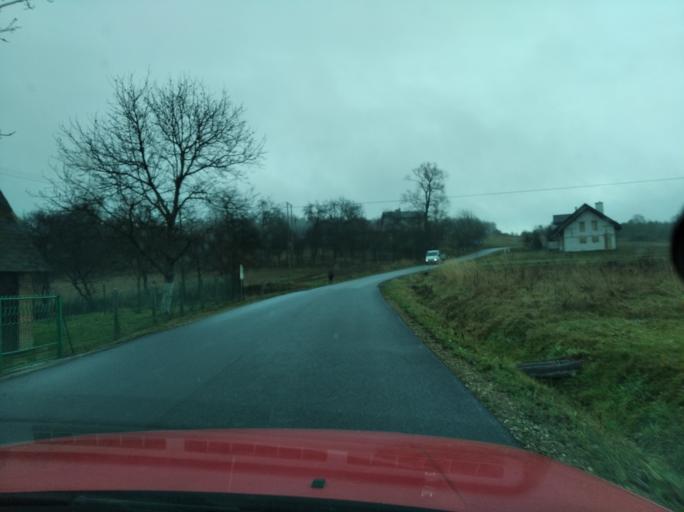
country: PL
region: Subcarpathian Voivodeship
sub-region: Powiat jaroslawski
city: Jodlowka
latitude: 49.8771
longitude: 22.4254
